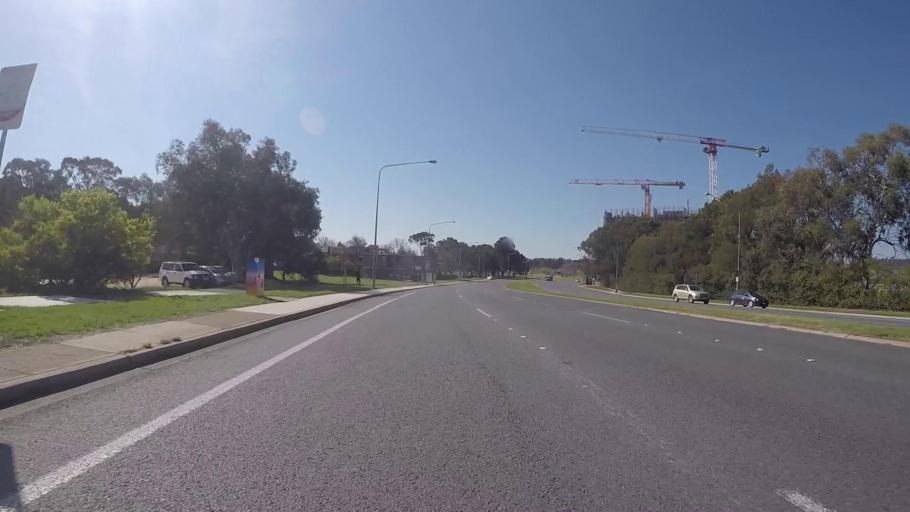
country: AU
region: Australian Capital Territory
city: Forrest
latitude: -35.3398
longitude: 149.0825
